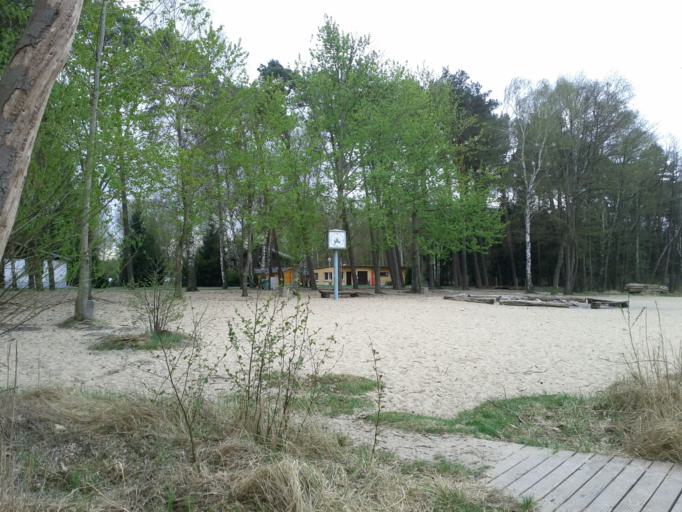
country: DE
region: Brandenburg
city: Spreenhagen
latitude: 52.3818
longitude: 13.8502
